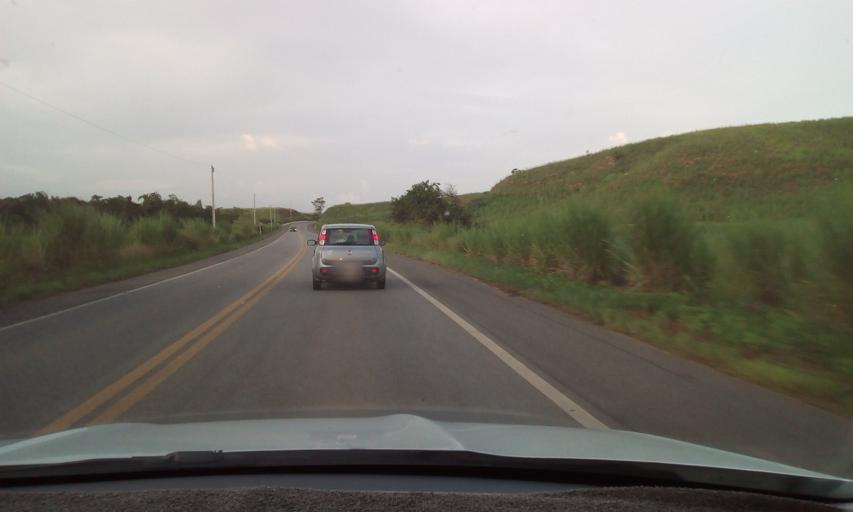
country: BR
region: Pernambuco
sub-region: Vicencia
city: Vicencia
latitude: -7.6336
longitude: -35.2518
